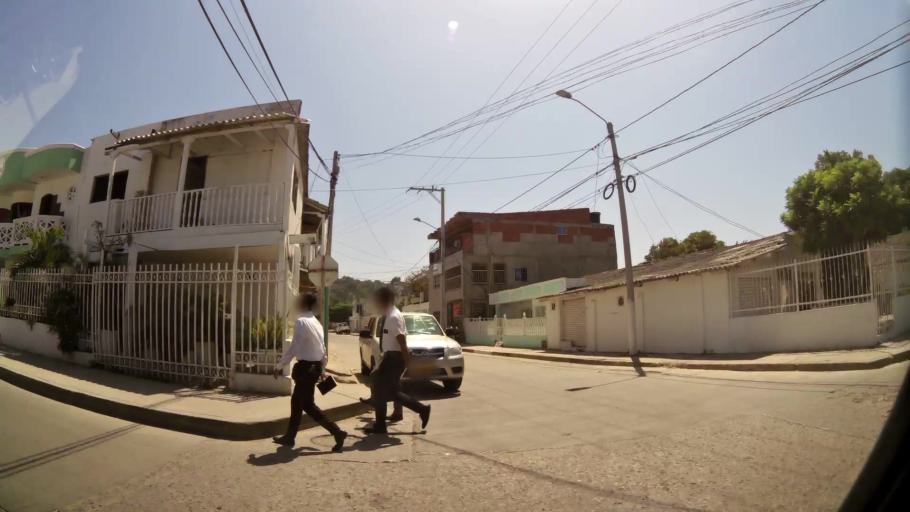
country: CO
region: Bolivar
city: Cartagena
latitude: 10.4339
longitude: -75.5319
